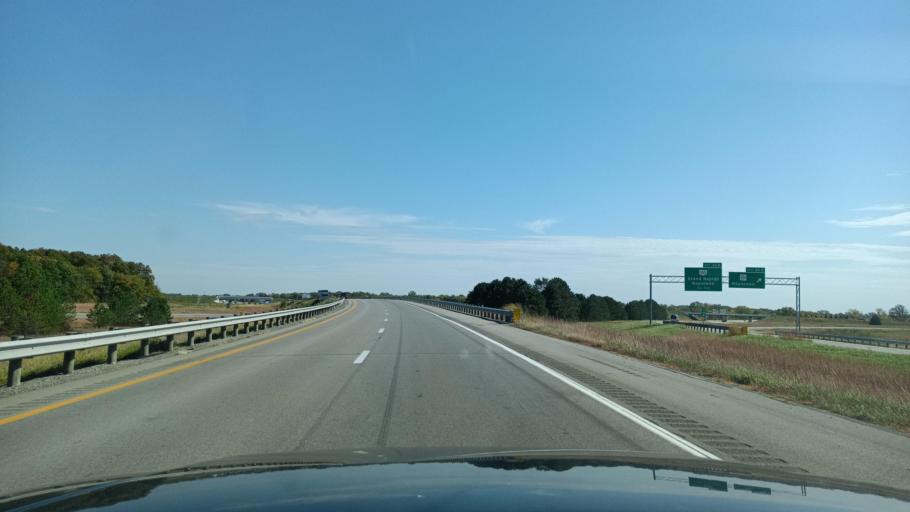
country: US
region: Ohio
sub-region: Henry County
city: Napoleon
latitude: 41.4160
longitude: -84.0664
